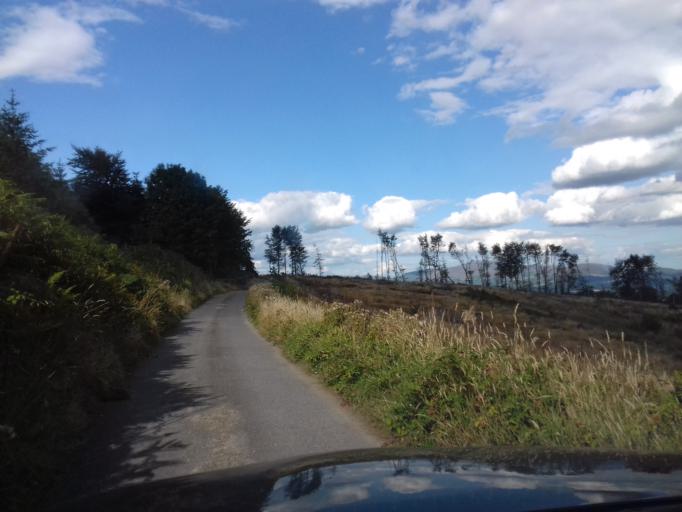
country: IE
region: Leinster
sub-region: Kilkenny
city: Graiguenamanagh
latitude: 52.5585
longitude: -7.0143
